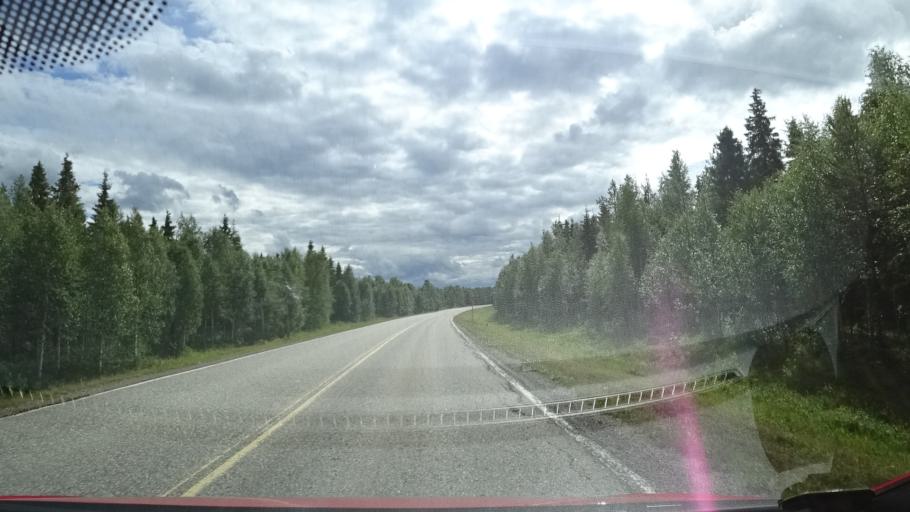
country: FI
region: Lapland
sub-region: Tunturi-Lappi
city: Kittilae
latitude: 67.4677
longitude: 24.9476
